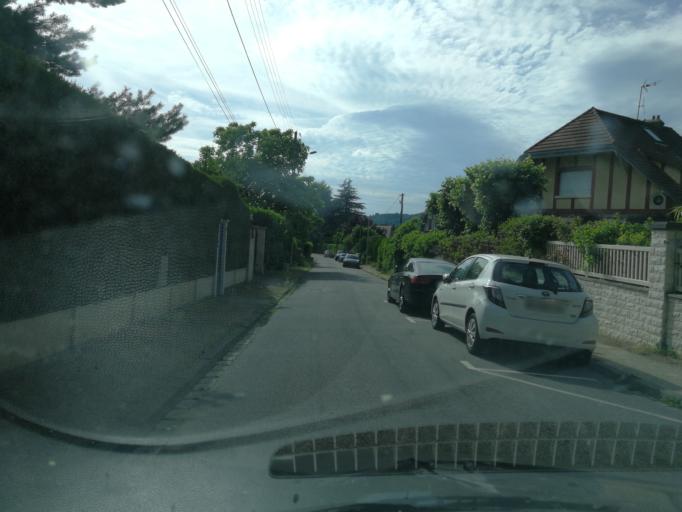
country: FR
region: Ile-de-France
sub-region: Departement des Yvelines
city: Saint-Remy-les-Chevreuse
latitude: 48.7006
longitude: 2.0740
